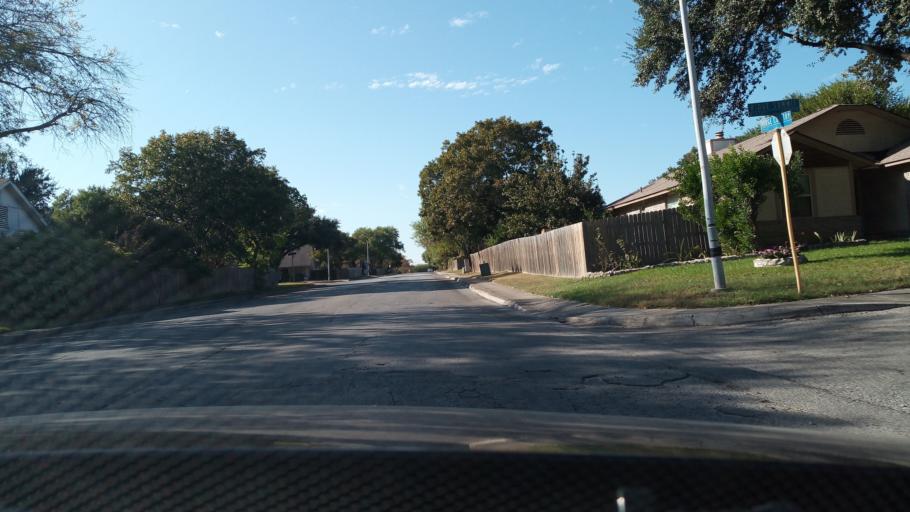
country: US
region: Texas
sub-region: Bexar County
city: Windcrest
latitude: 29.5562
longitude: -98.4332
